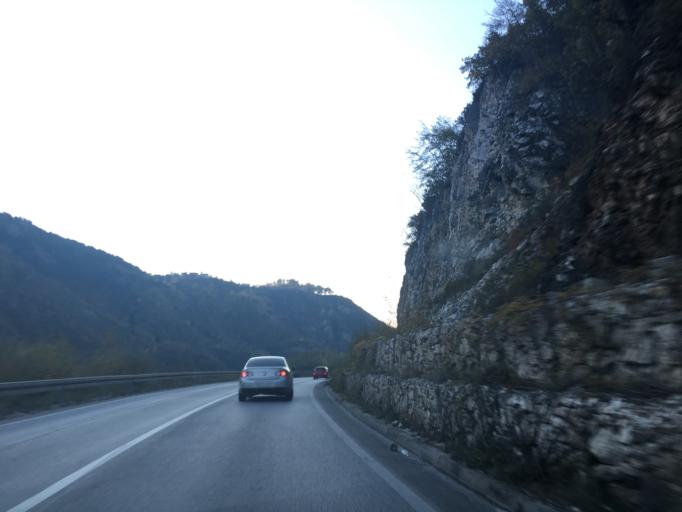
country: BA
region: Federation of Bosnia and Herzegovina
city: Kobilja Glava
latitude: 43.8466
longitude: 18.4706
